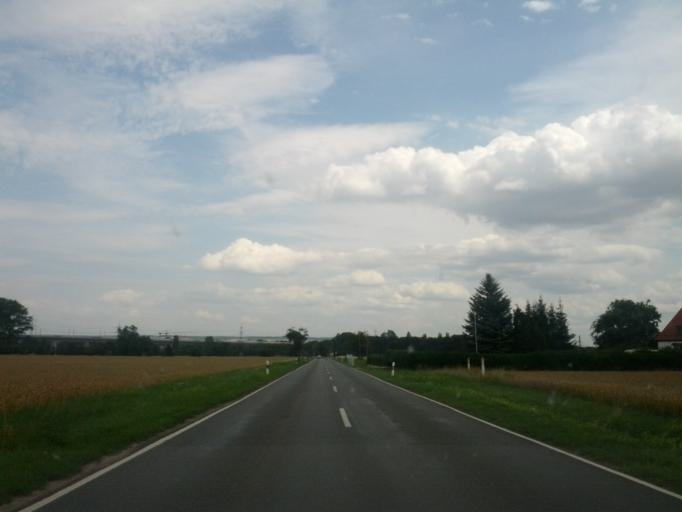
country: DE
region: Thuringia
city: Ichtershausen
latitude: 50.8873
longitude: 10.9571
